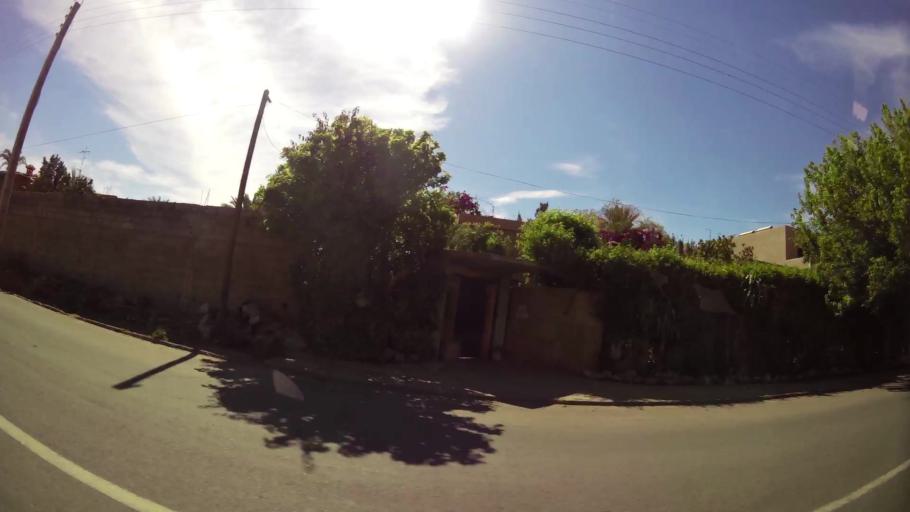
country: MA
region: Marrakech-Tensift-Al Haouz
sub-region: Marrakech
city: Marrakesh
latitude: 31.6432
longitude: -8.0470
